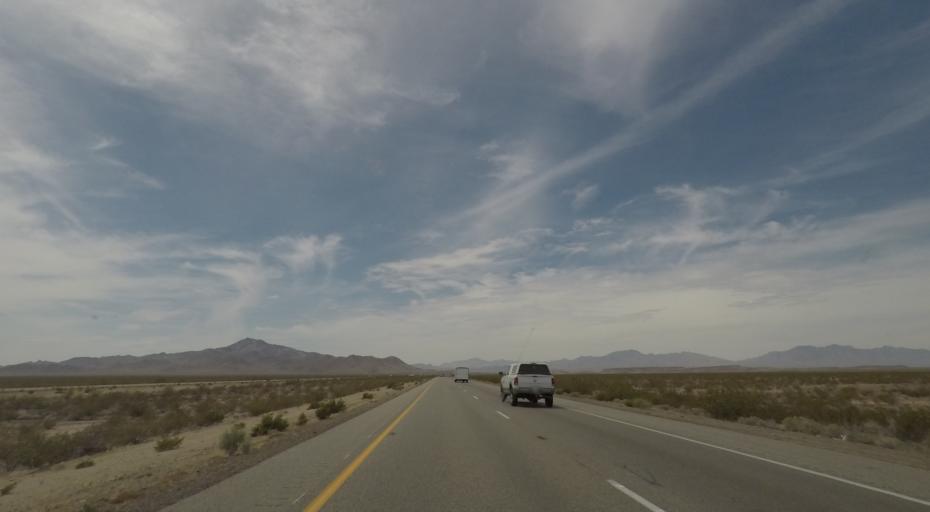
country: US
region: California
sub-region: San Bernardino County
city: Needles
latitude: 34.8064
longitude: -115.2577
